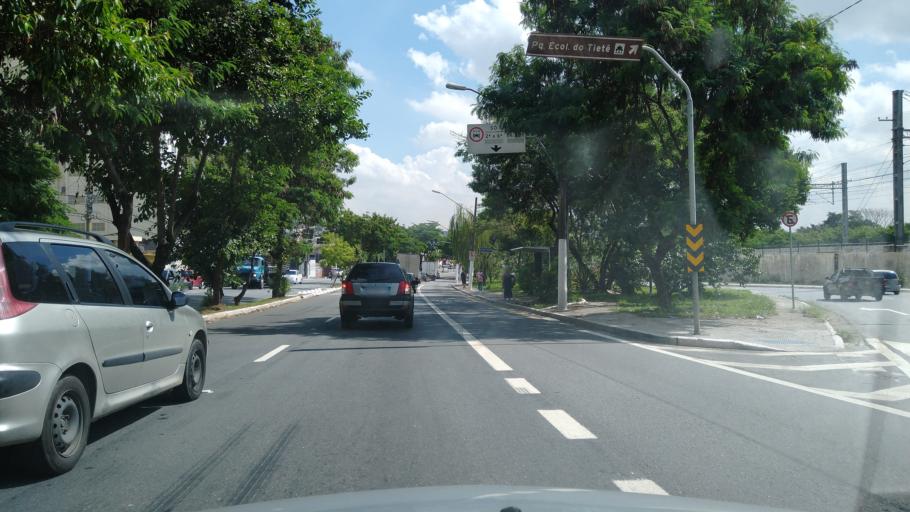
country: BR
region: Sao Paulo
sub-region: Guarulhos
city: Guarulhos
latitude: -23.4994
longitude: -46.5223
